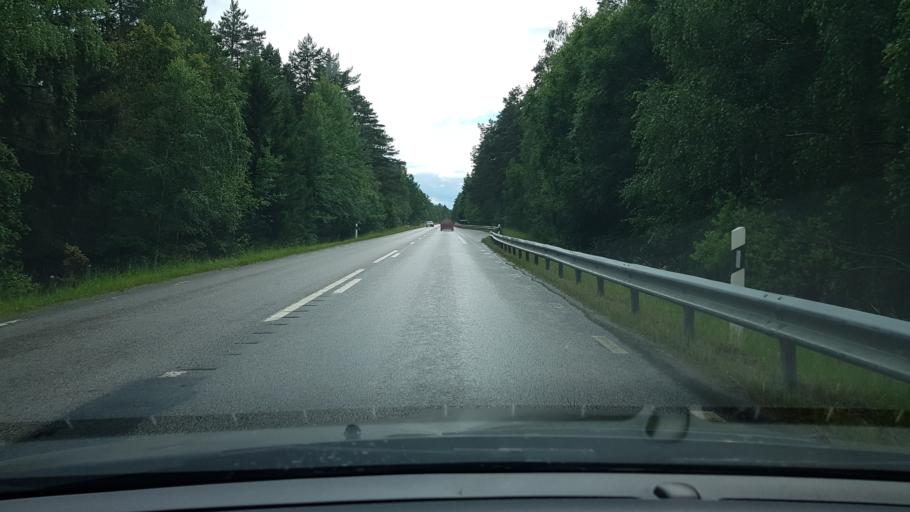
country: SE
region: Uppsala
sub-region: Uppsala Kommun
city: Saevja
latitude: 59.8020
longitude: 17.6840
